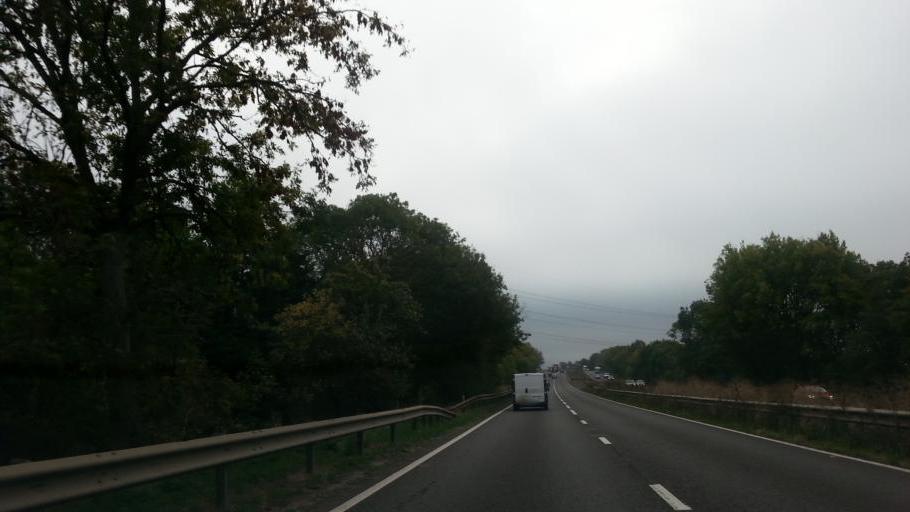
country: GB
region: England
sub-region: Peterborough
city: Upton
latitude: 52.5636
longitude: -0.3804
